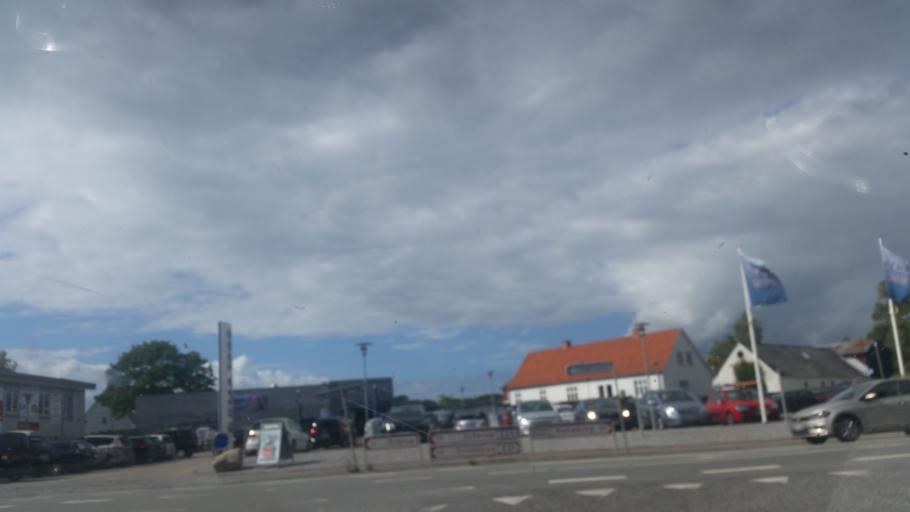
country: DK
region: Zealand
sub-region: Odsherred Kommune
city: Horve
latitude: 55.8035
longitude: 11.4399
